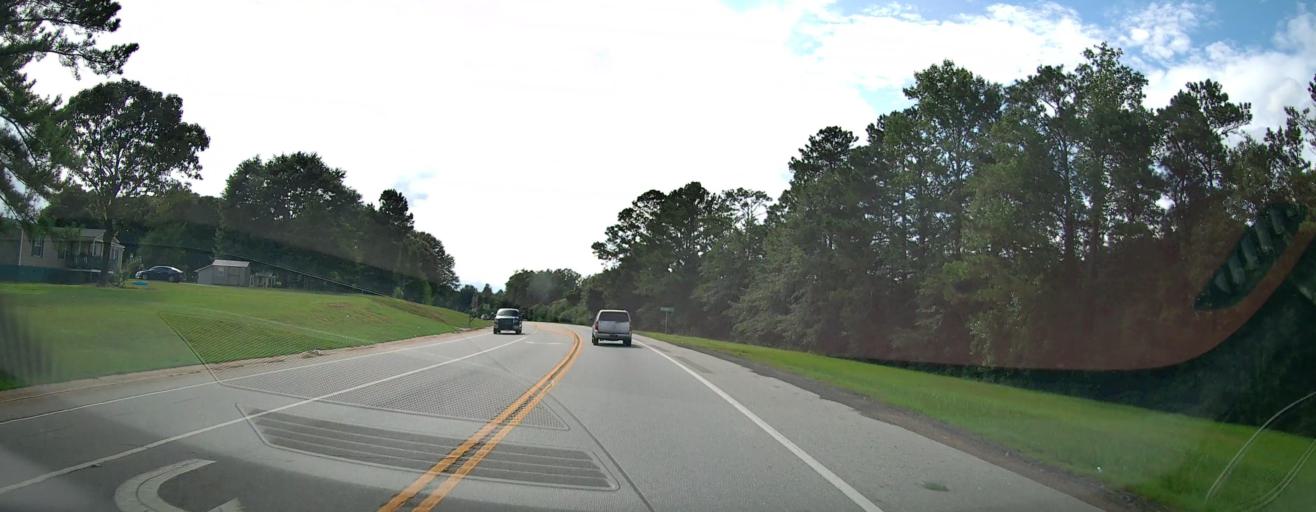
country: US
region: Georgia
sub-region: Upson County
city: Hannahs Mill
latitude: 32.9931
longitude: -84.5087
